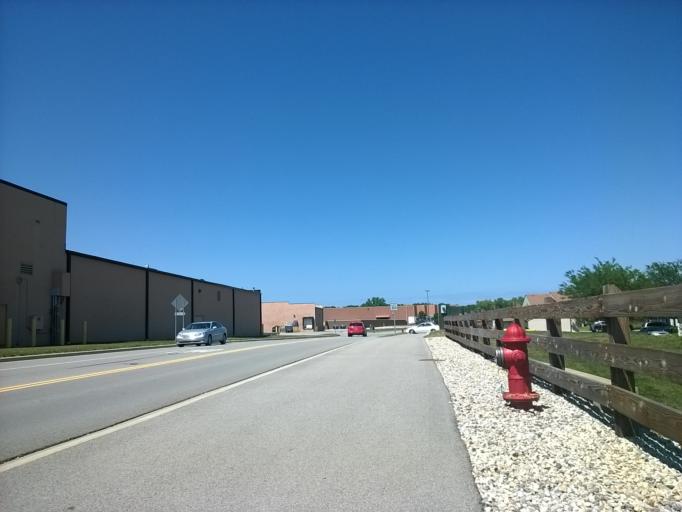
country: US
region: Indiana
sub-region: Hamilton County
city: Carmel
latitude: 40.0037
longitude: -86.1233
